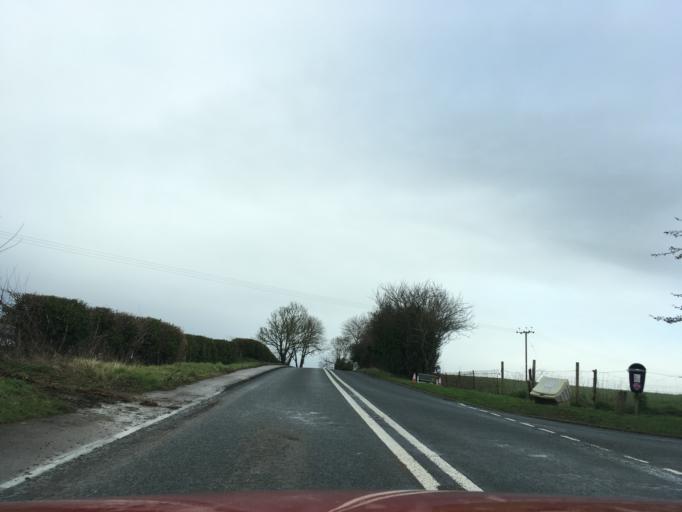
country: GB
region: England
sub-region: Worcestershire
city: Evesham
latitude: 52.0453
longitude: -1.9752
